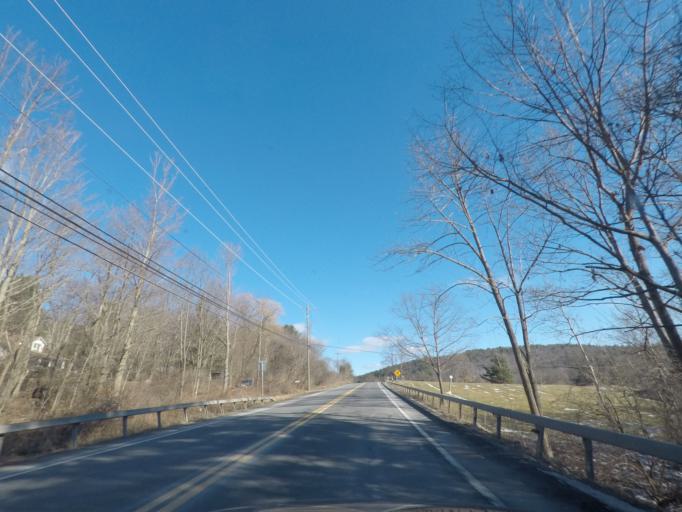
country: US
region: New York
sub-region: Columbia County
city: Chatham
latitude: 42.3200
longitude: -73.5298
